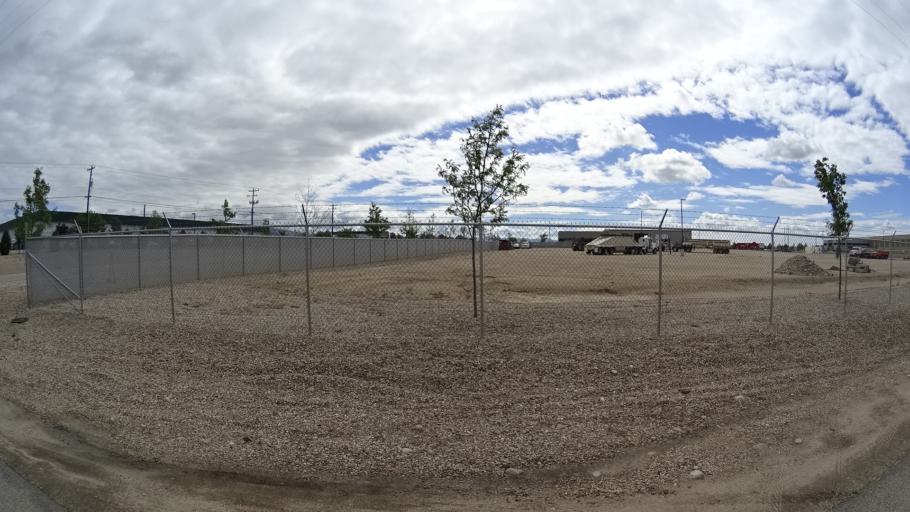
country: US
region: Idaho
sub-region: Ada County
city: Boise
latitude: 43.5473
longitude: -116.1935
